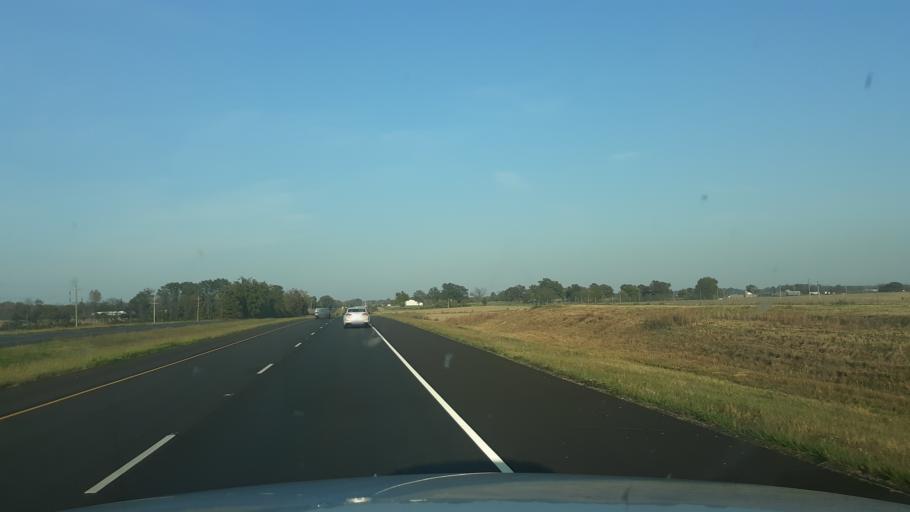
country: US
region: Illinois
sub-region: Saline County
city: Eldorado
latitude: 37.7935
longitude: -88.4743
